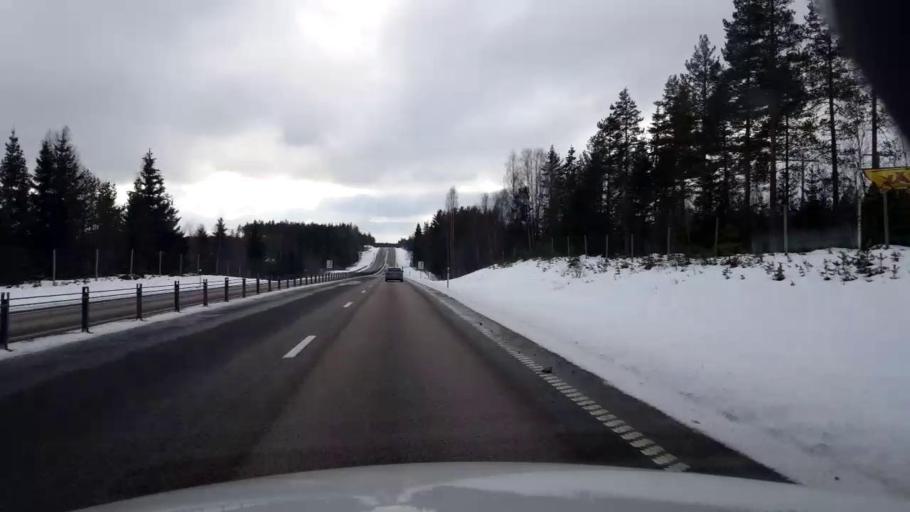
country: SE
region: Gaevleborg
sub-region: Hudiksvalls Kommun
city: Hudiksvall
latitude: 61.8238
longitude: 17.1915
